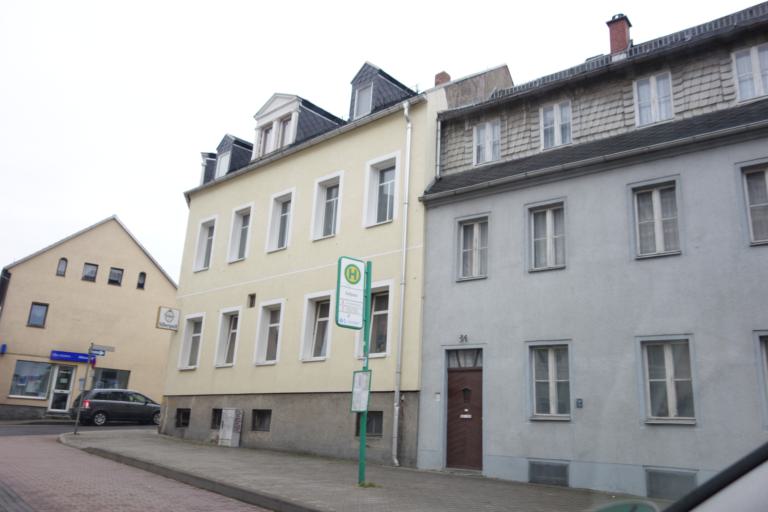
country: DE
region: Saxony
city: Freiberg
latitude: 50.9111
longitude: 13.3484
